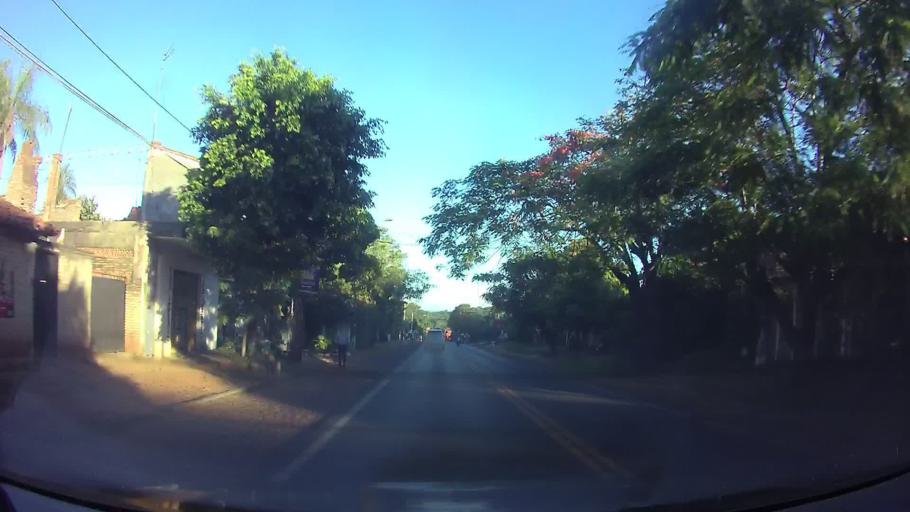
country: PY
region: Central
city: Aregua
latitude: -25.3020
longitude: -57.4050
